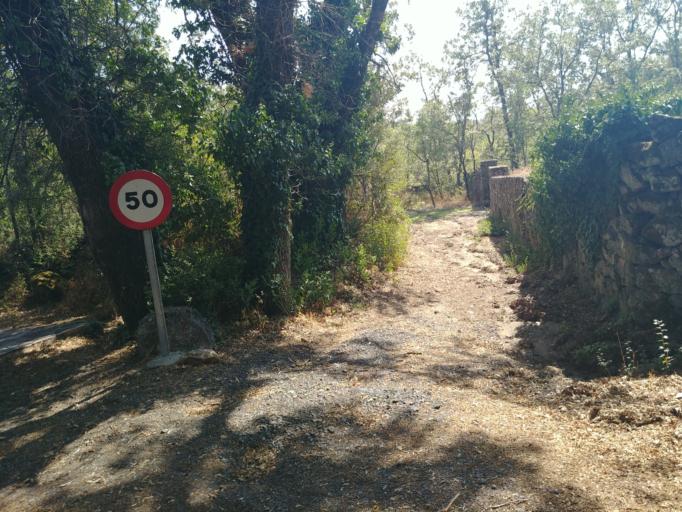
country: ES
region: Extremadura
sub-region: Provincia de Caceres
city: Garganta la Olla
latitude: 40.1123
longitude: -5.7391
